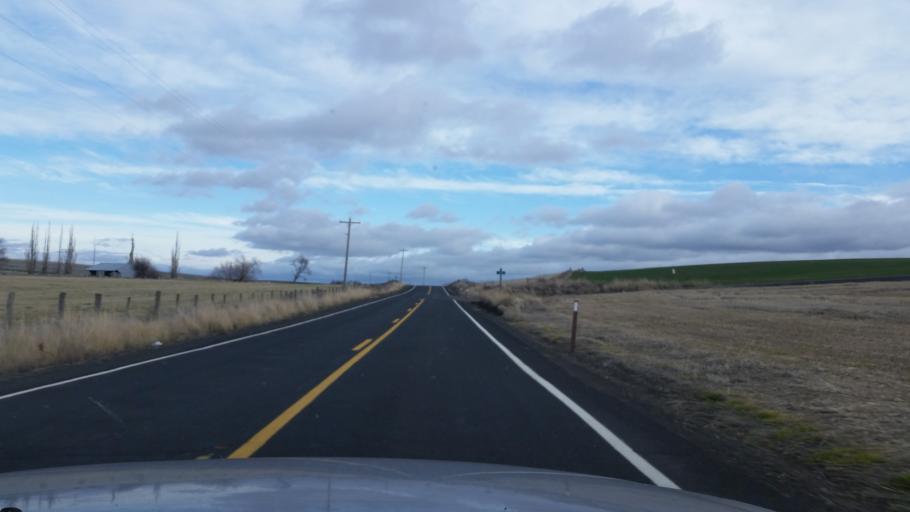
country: US
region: Washington
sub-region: Lincoln County
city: Davenport
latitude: 47.3487
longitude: -118.0799
